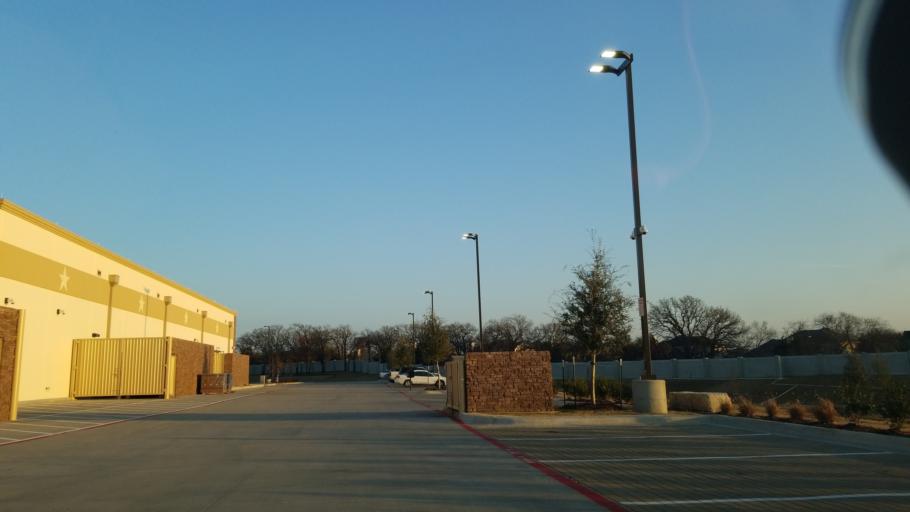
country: US
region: Texas
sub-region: Denton County
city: Corinth
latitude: 33.1792
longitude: -97.1032
